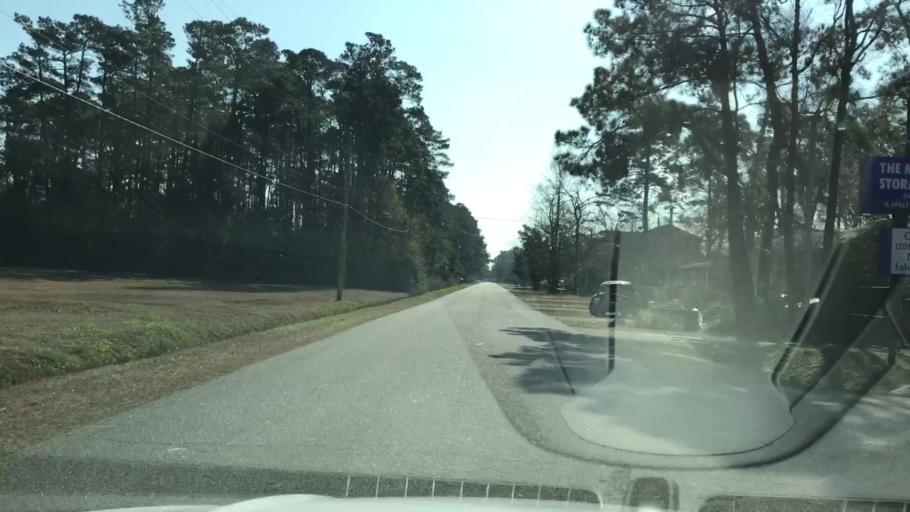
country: US
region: South Carolina
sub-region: Horry County
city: Garden City
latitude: 33.5881
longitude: -79.0067
